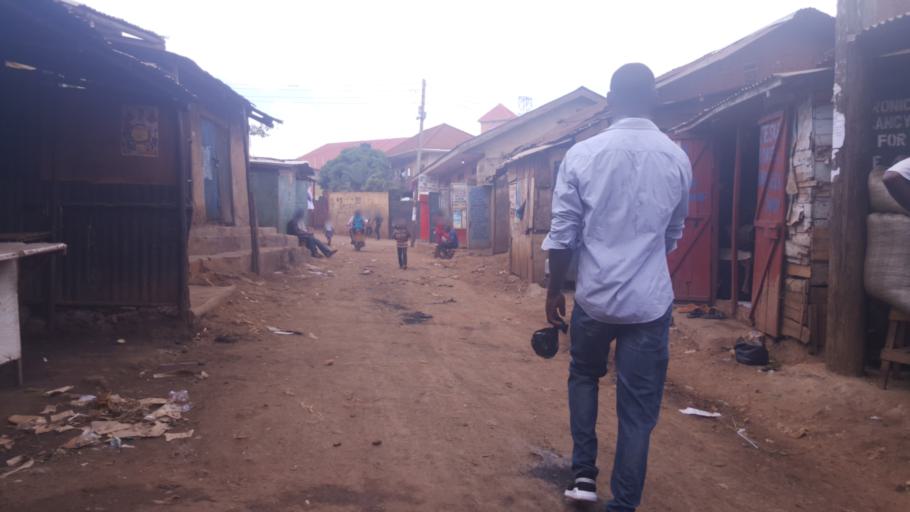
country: UG
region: Central Region
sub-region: Kampala District
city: Kampala
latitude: 0.3040
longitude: 32.5788
